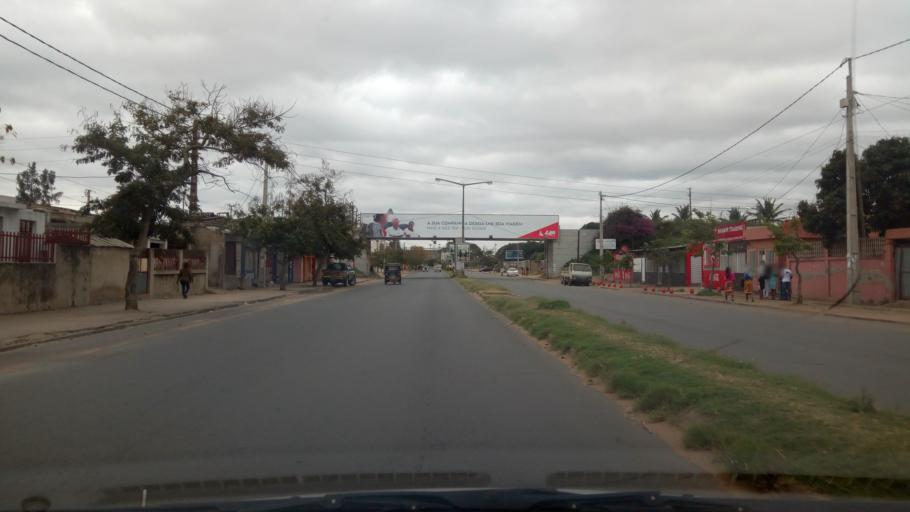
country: MZ
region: Maputo City
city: Maputo
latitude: -25.9301
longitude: 32.5782
